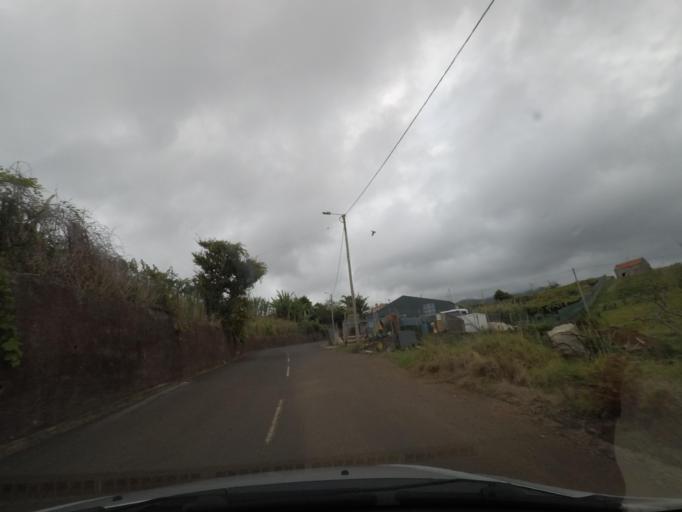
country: PT
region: Madeira
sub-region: Santana
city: Santana
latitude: 32.8179
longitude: -16.8841
